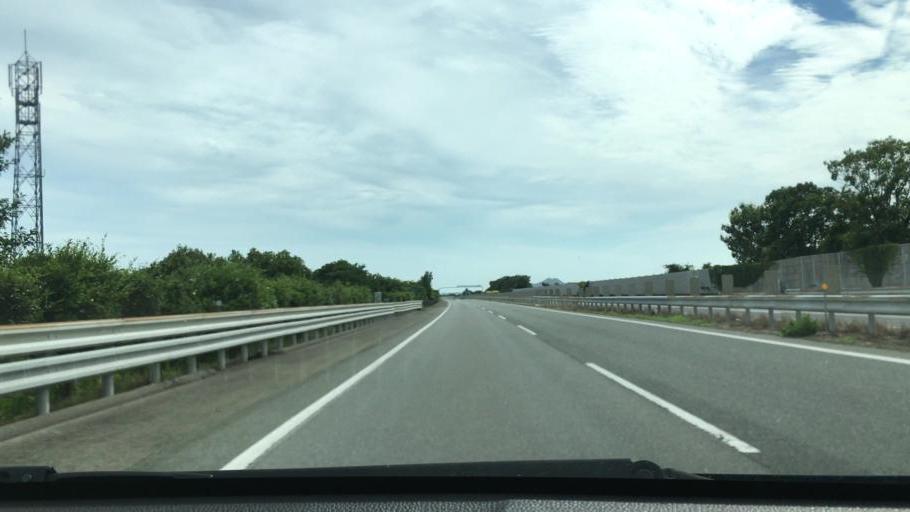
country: JP
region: Yamaguchi
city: Hofu
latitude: 34.0621
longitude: 131.5464
